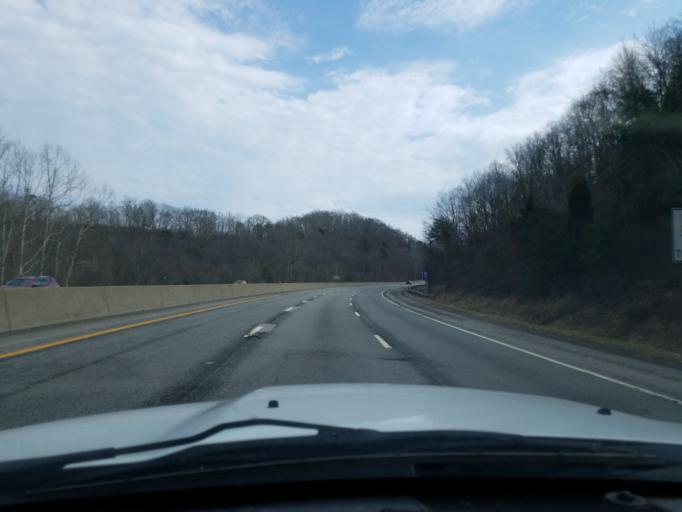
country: US
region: West Virginia
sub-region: Kanawha County
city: Cross Lanes
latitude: 38.4268
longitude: -81.8145
